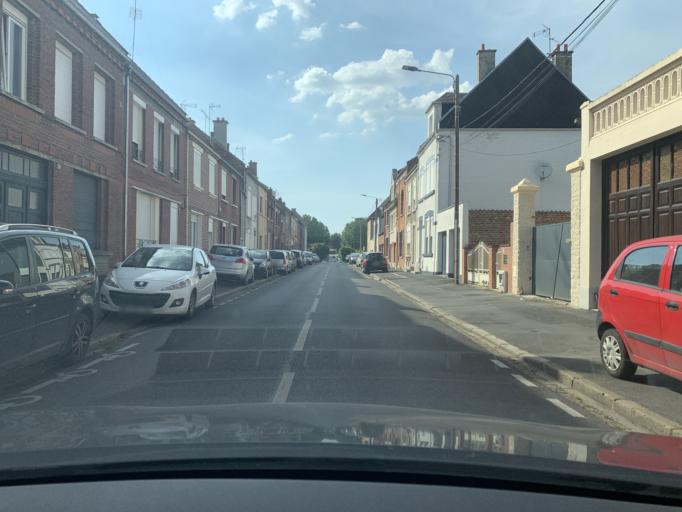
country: FR
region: Nord-Pas-de-Calais
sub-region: Departement du Nord
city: Cambrai
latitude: 50.1682
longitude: 3.2492
